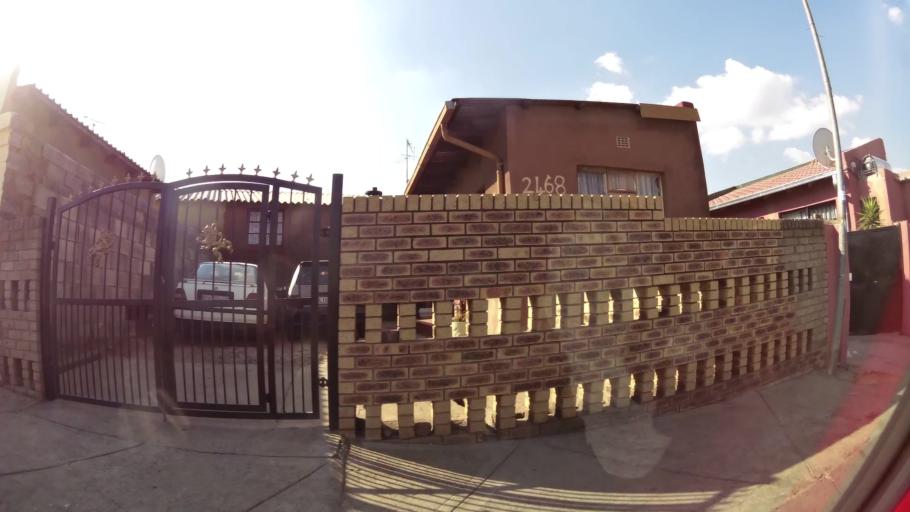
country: ZA
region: Gauteng
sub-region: City of Johannesburg Metropolitan Municipality
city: Soweto
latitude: -26.2511
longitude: 27.9456
